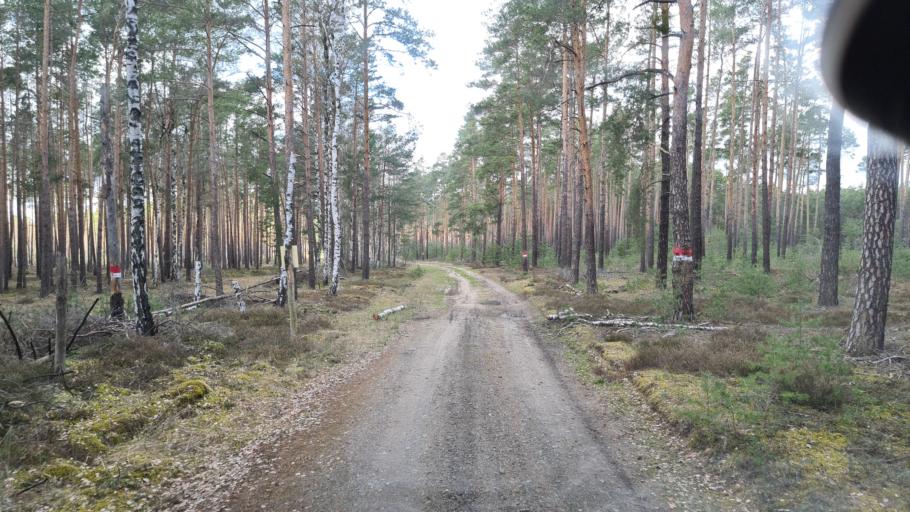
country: DE
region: Brandenburg
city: Schonborn
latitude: 51.6517
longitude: 13.4733
